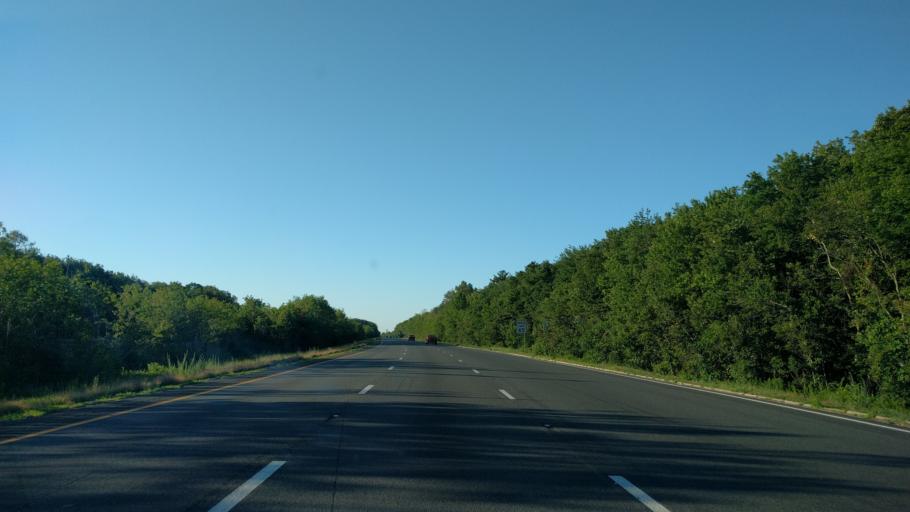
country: US
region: Massachusetts
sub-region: Worcester County
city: Milford
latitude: 42.1440
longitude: -71.4835
